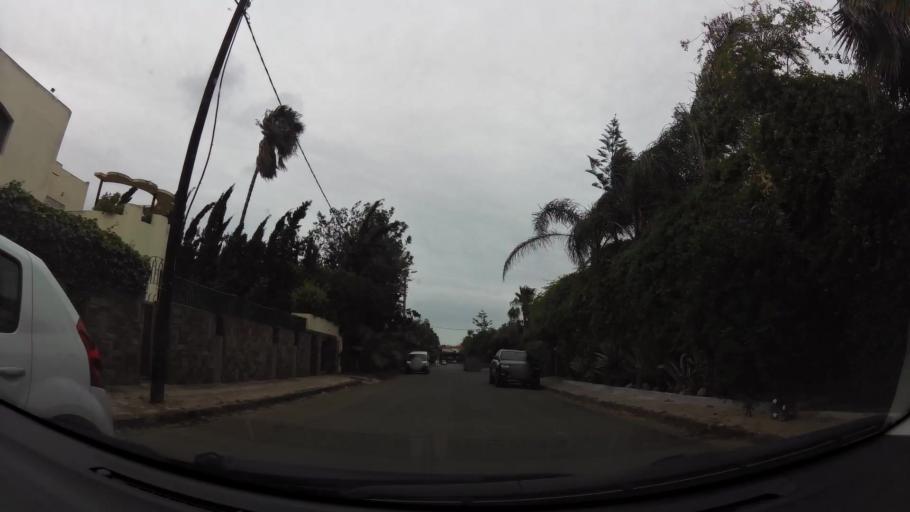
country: MA
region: Grand Casablanca
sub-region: Casablanca
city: Casablanca
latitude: 33.5836
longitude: -7.6533
